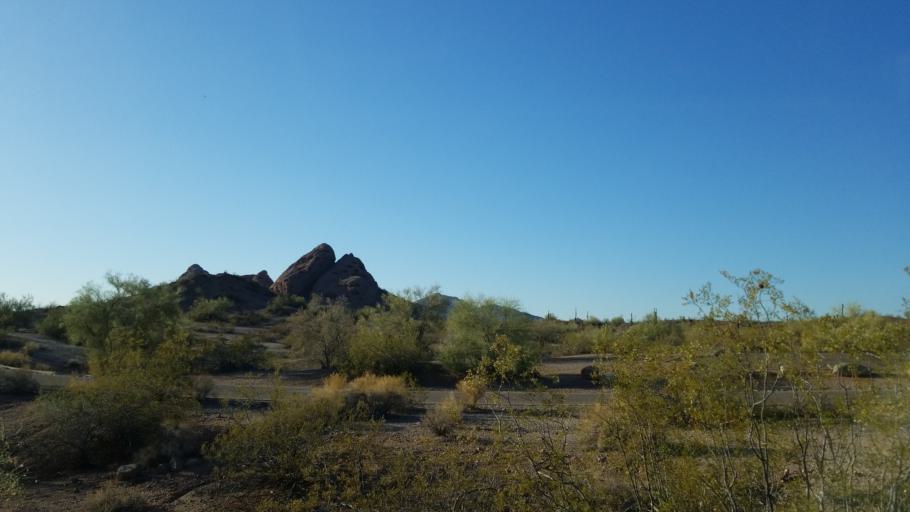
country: US
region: Arizona
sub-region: Maricopa County
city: Tempe Junction
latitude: 33.4561
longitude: -111.9479
